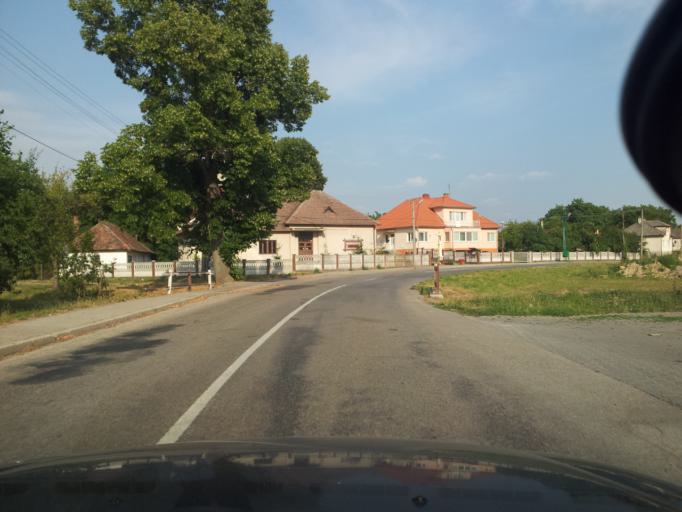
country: SK
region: Nitriansky
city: Banovce nad Bebravou
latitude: 48.8049
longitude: 18.1937
